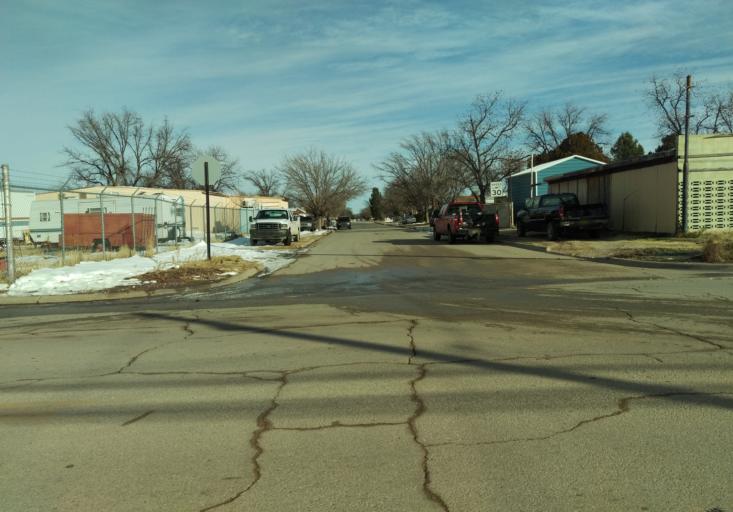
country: US
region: New Mexico
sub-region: Eddy County
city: Carlsbad
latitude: 32.4215
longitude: -104.2495
